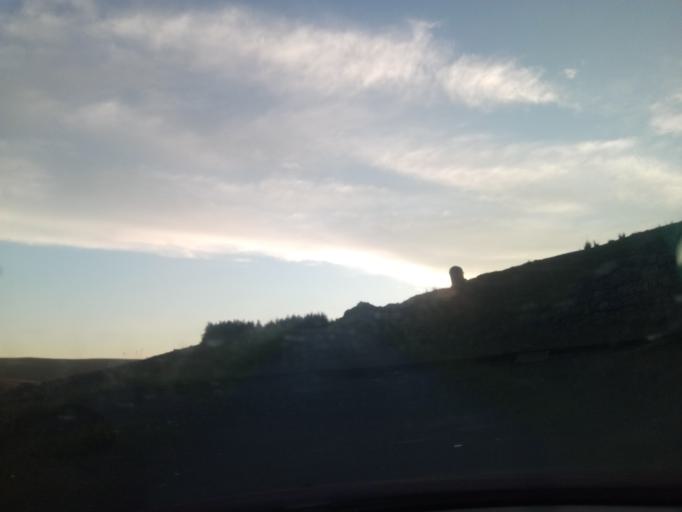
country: GB
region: England
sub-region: Northumberland
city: Bardon Mill
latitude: 54.7987
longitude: -2.3457
